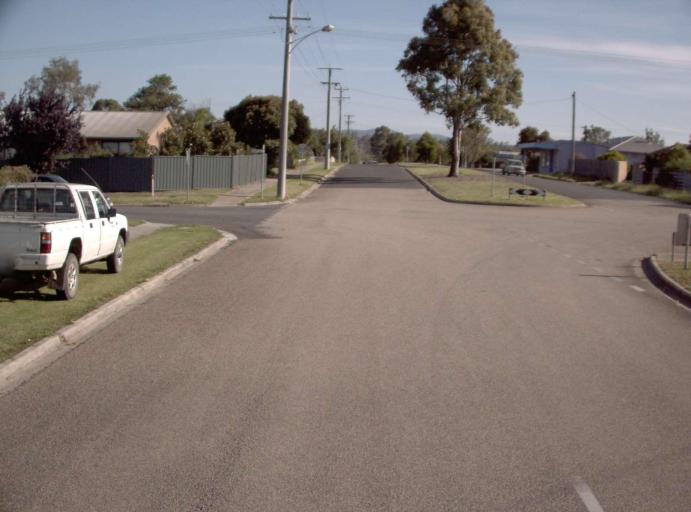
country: AU
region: Victoria
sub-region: East Gippsland
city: Lakes Entrance
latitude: -37.6978
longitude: 148.4570
